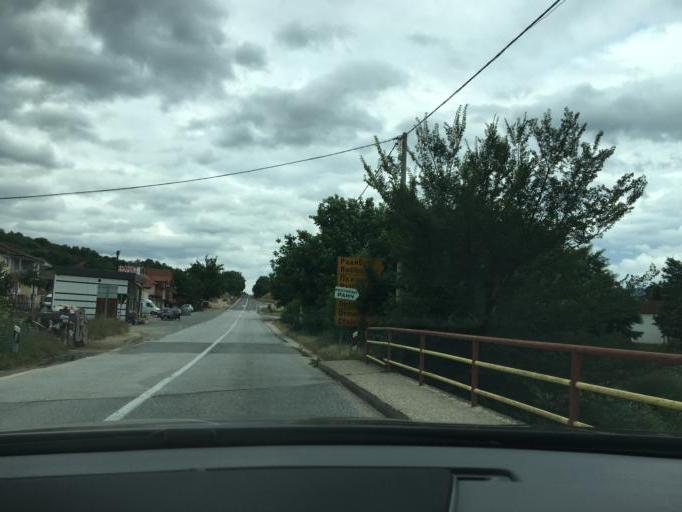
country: MK
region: Opstina Rankovce
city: Rankovce
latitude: 42.1677
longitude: 22.1191
